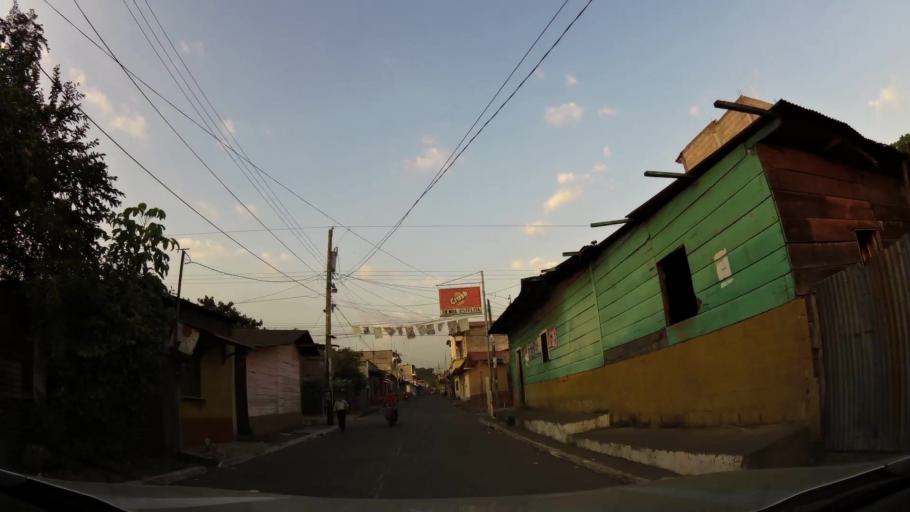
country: GT
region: Retalhuleu
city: San Sebastian
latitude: 14.5605
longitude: -91.6502
